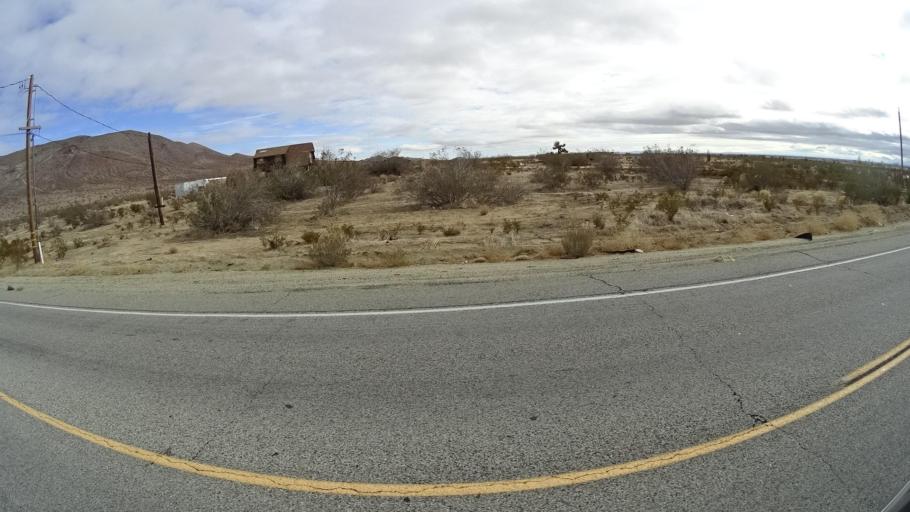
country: US
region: California
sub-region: Kern County
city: Rosamond
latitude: 34.8713
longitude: -118.2910
